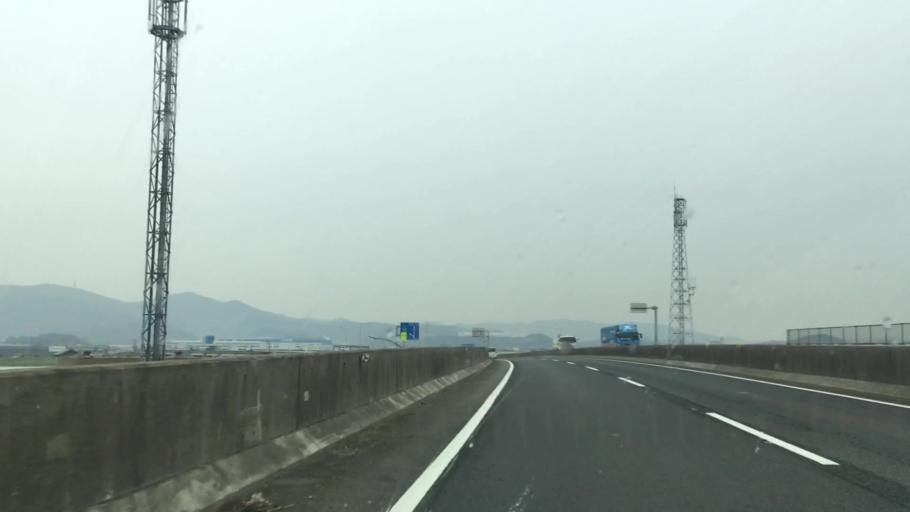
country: JP
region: Aichi
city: Nishio
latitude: 34.8733
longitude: 137.0827
